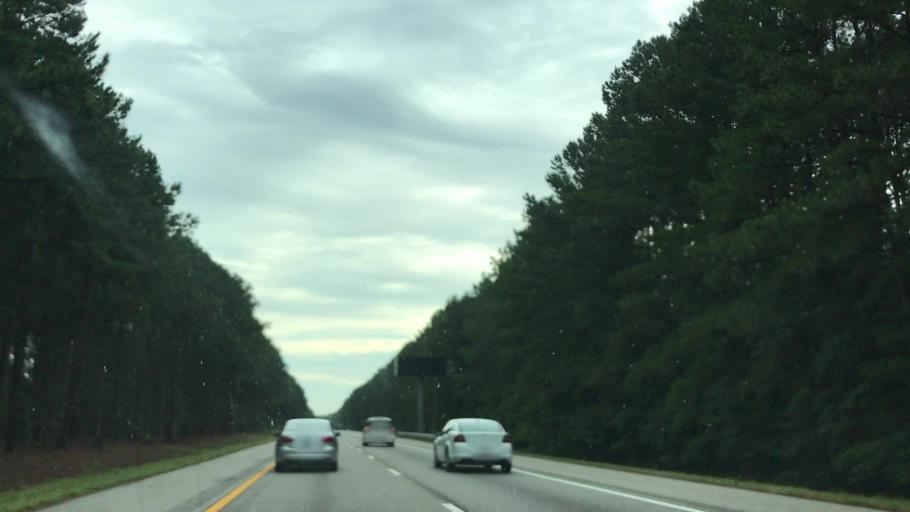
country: US
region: North Carolina
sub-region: Wilson County
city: Lucama
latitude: 35.6775
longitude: -78.0681
